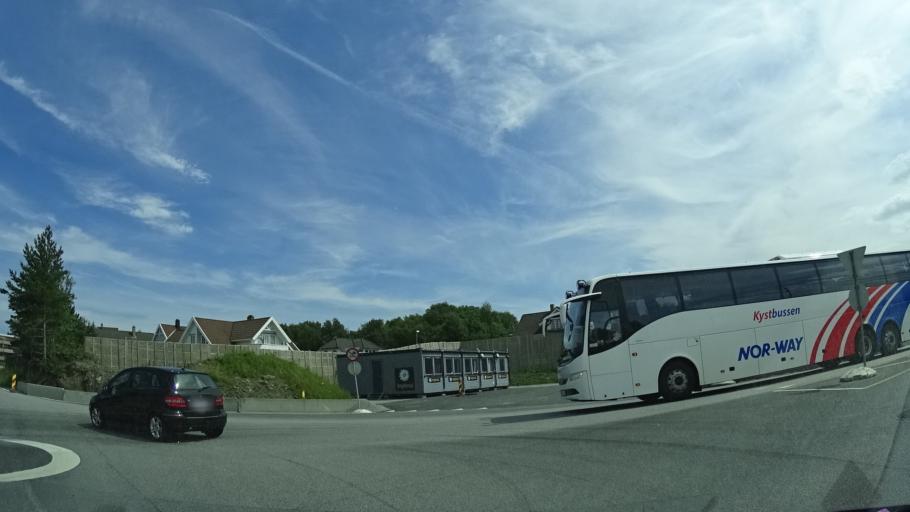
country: NO
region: Rogaland
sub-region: Stavanger
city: Stavanger
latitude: 58.9788
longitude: 5.6873
